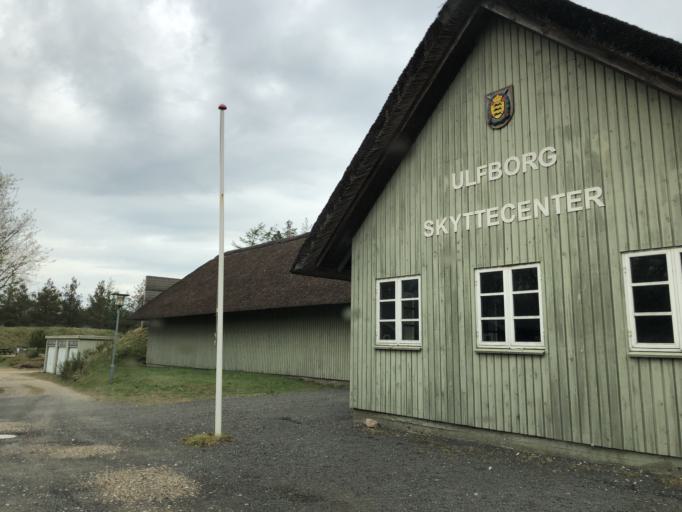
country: DK
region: Central Jutland
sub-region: Holstebro Kommune
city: Ulfborg
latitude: 56.2600
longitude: 8.3488
